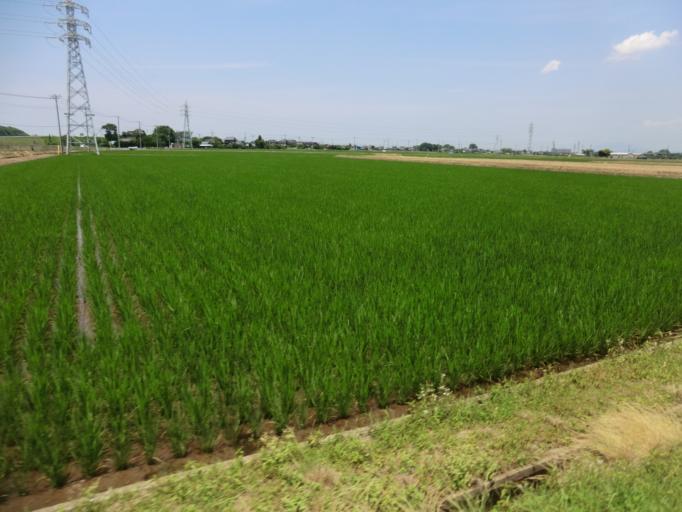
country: JP
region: Ibaraki
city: Moriya
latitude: 35.9439
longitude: 140.0326
